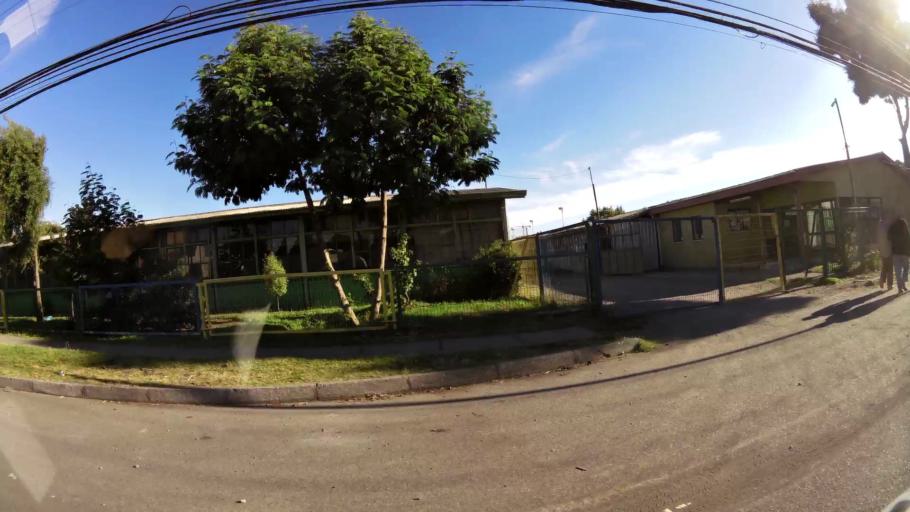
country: CL
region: Biobio
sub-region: Provincia de Concepcion
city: Concepcion
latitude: -36.8327
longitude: -73.1015
